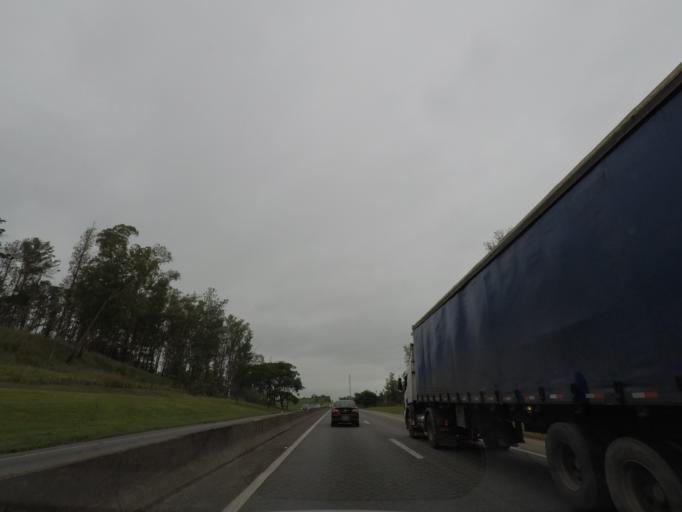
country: BR
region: Sao Paulo
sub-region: Pindamonhangaba
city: Pindamonhangaba
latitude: -22.9768
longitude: -45.4535
